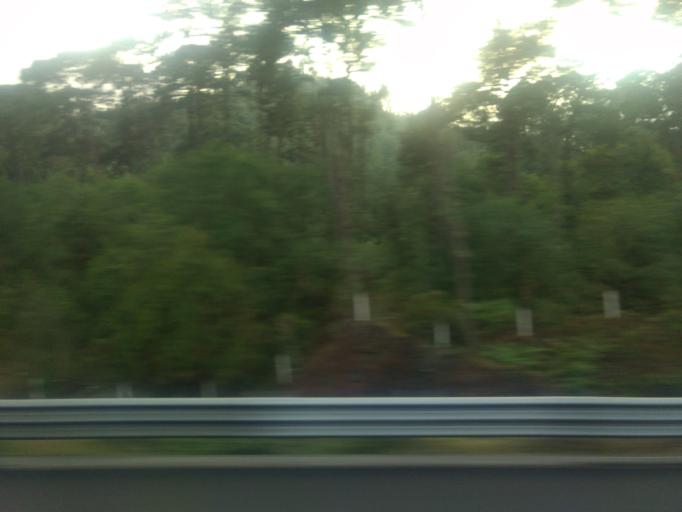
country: MX
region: Veracruz
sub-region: Acajete
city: La Joya
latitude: 19.6285
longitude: -97.0279
